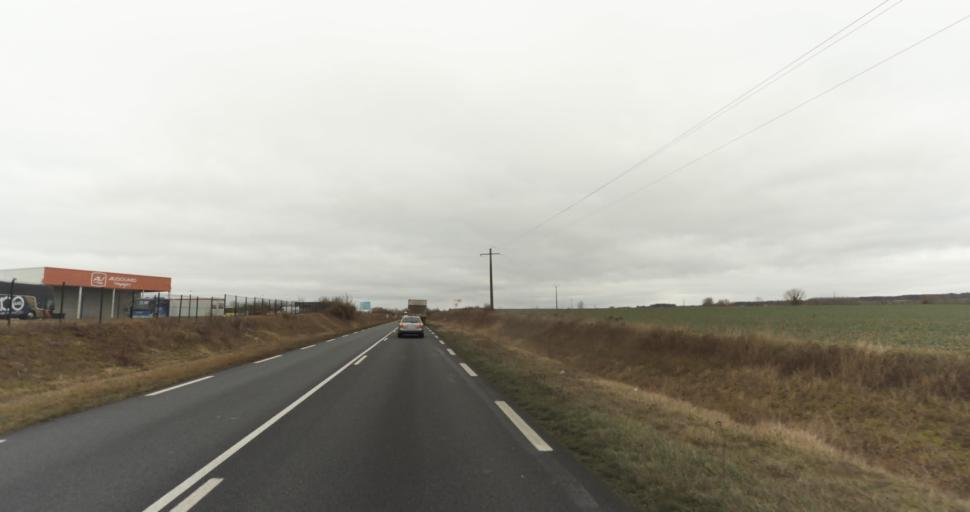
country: FR
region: Pays de la Loire
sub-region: Departement de Maine-et-Loire
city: Doue-la-Fontaine
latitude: 47.1904
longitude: -0.2434
